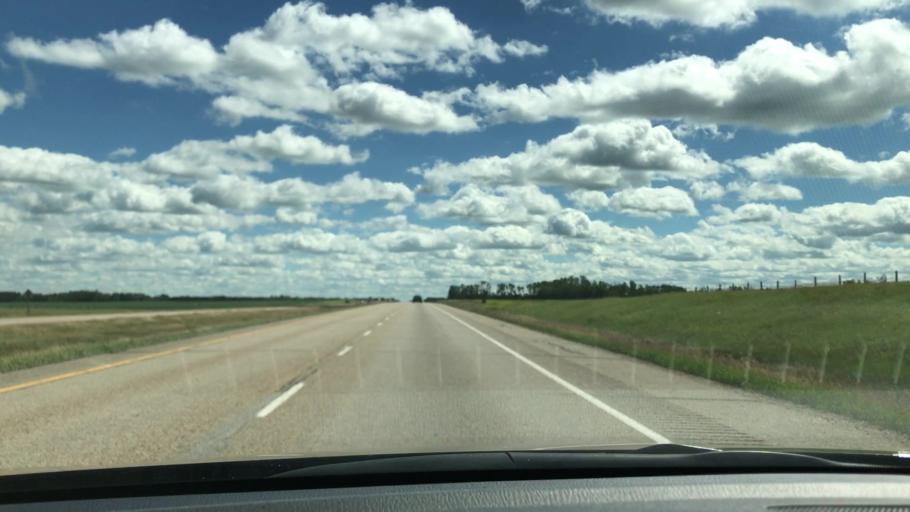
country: CA
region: Alberta
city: Millet
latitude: 53.1332
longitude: -113.5983
